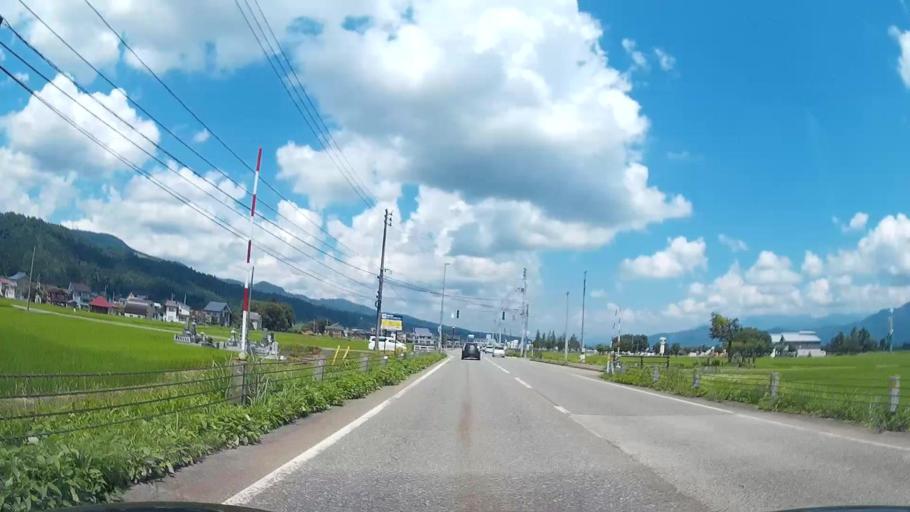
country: JP
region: Niigata
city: Shiozawa
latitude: 37.0010
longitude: 138.8156
